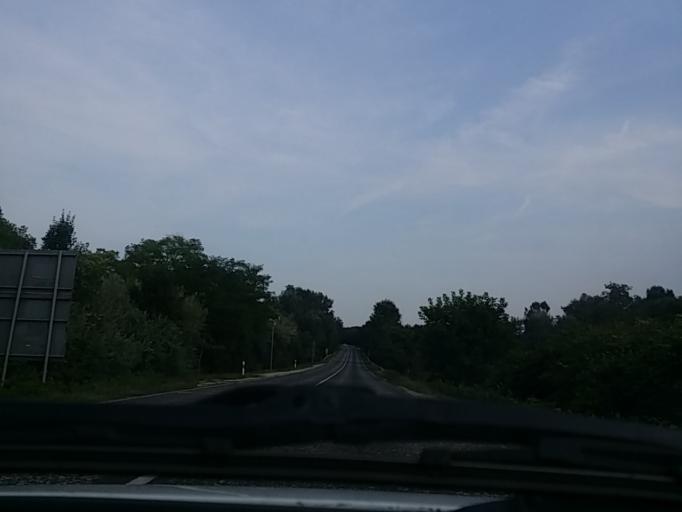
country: HU
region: Fejer
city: Etyek
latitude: 47.4907
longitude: 18.7641
